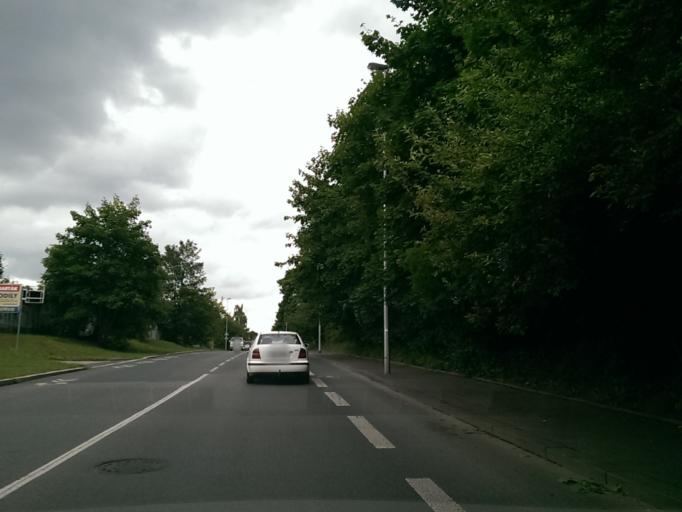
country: CZ
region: Praha
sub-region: Praha 4
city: Hodkovicky
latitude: 50.0306
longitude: 14.4174
